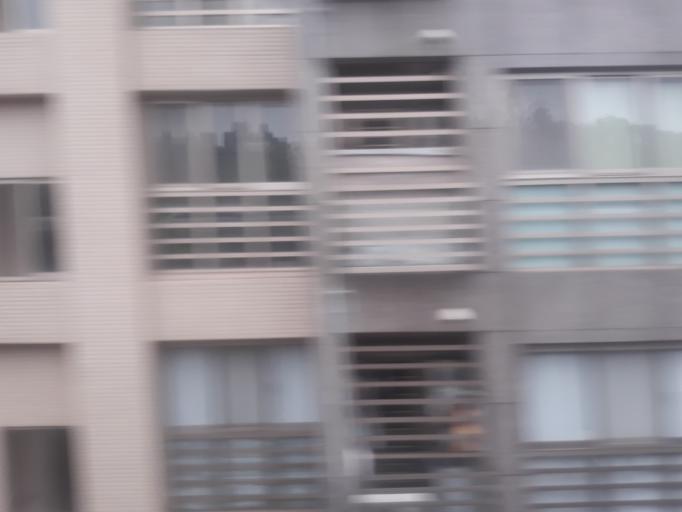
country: TW
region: Taipei
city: Taipei
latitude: 24.9985
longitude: 121.5690
